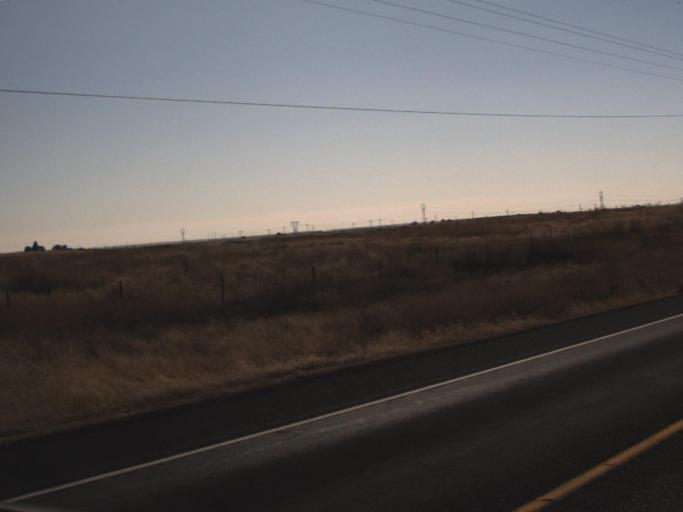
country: US
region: Washington
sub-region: Franklin County
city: Connell
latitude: 46.6577
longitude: -119.0064
